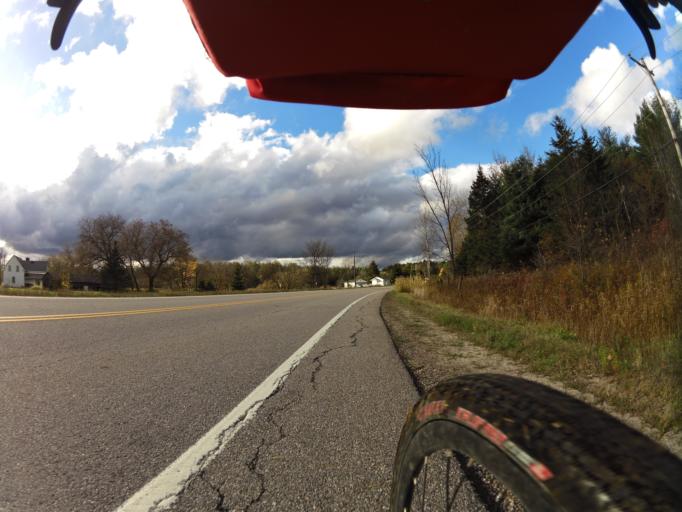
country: CA
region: Quebec
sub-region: Outaouais
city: Wakefield
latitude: 45.6631
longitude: -76.1331
